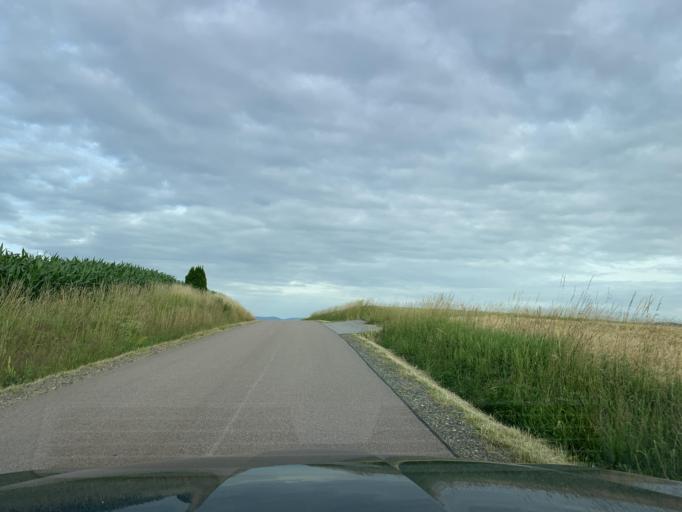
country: DE
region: Bavaria
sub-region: Upper Palatinate
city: Thanstein
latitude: 49.4076
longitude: 12.4530
